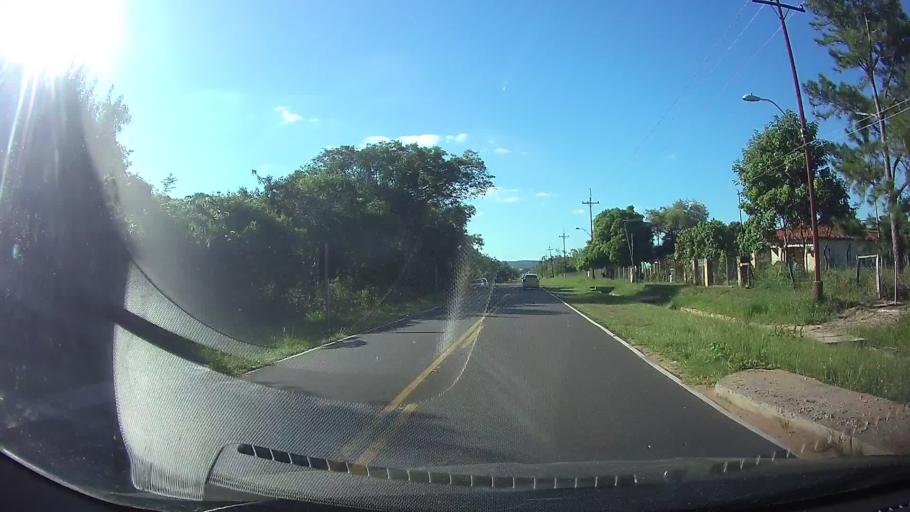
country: PY
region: Cordillera
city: Atyra
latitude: -25.2948
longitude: -57.1641
